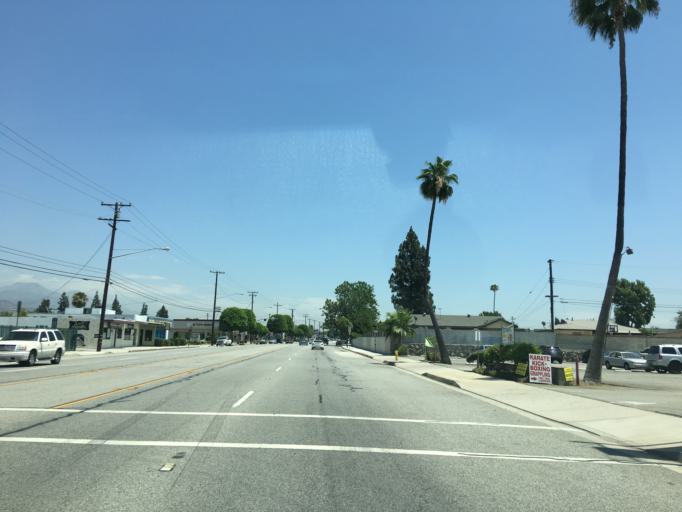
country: US
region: California
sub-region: Los Angeles County
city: Charter Oak
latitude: 34.1065
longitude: -117.8679
